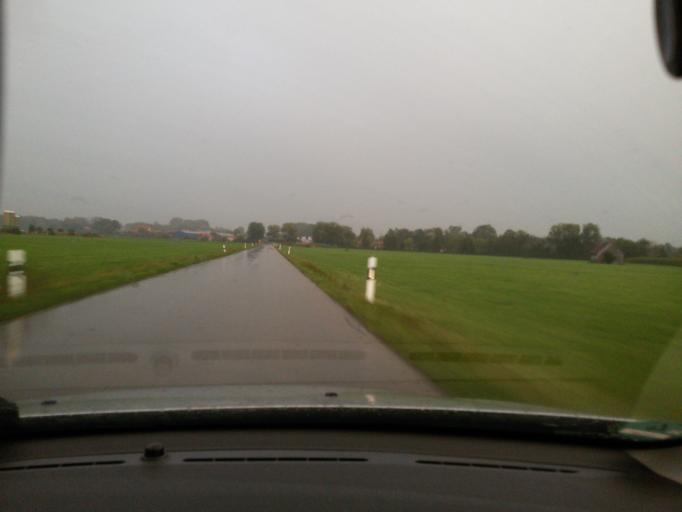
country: DE
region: Bavaria
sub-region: Swabia
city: Langerringen
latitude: 48.1529
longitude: 10.7431
